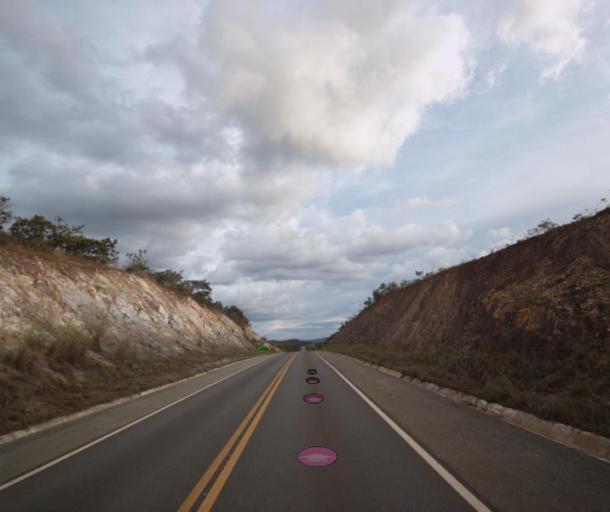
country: BR
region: Goias
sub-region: Barro Alto
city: Barro Alto
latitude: -14.8931
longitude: -48.6419
